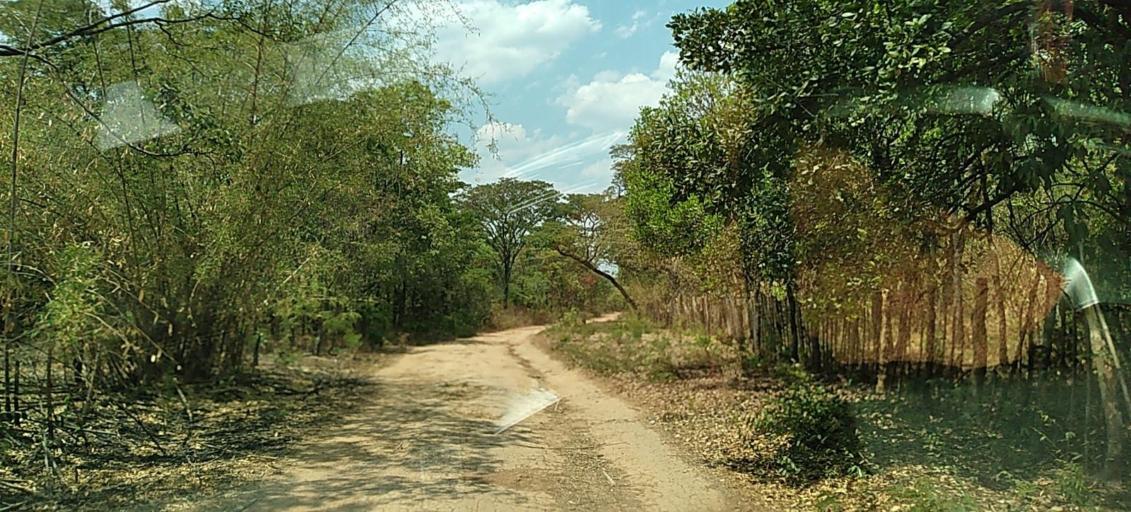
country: ZM
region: Copperbelt
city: Chililabombwe
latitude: -12.4849
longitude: 27.6412
